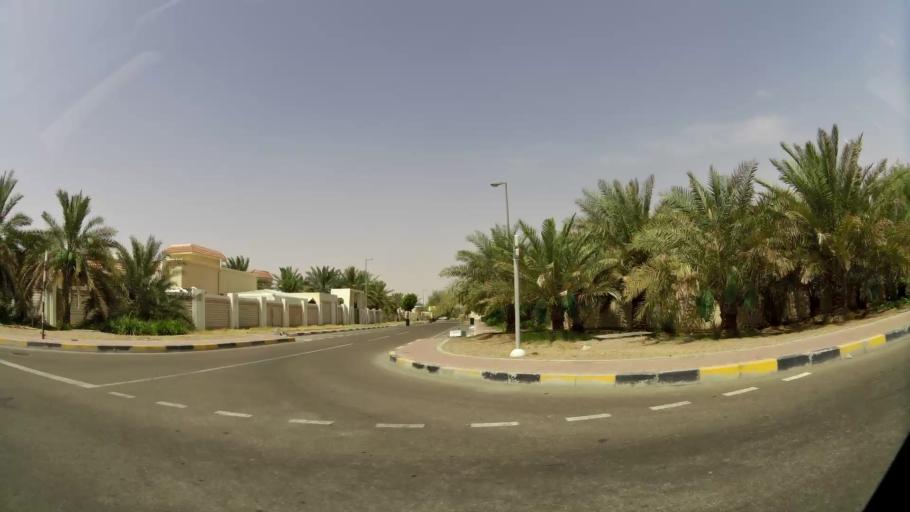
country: AE
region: Abu Dhabi
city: Al Ain
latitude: 24.1817
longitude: 55.7155
